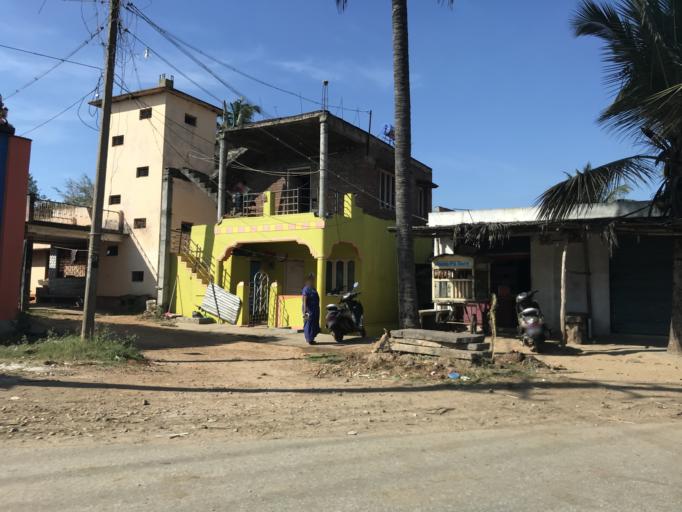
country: IN
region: Karnataka
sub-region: Mysore
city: Heggadadevankote
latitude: 12.1220
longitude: 76.4683
